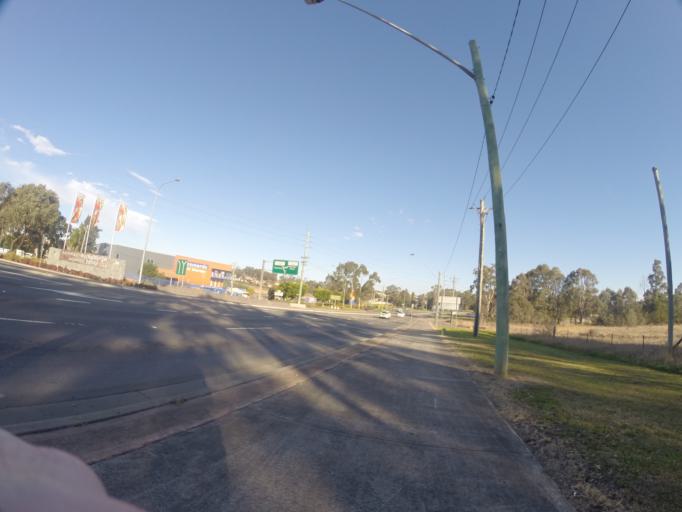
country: AU
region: New South Wales
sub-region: Fairfield
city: Horsley Park
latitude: -33.8494
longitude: 150.8764
